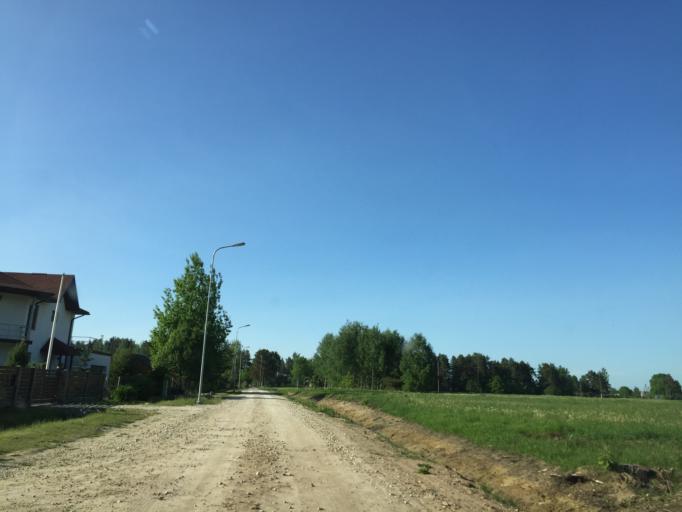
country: LV
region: Kekava
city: Kekava
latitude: 56.8222
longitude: 24.2626
